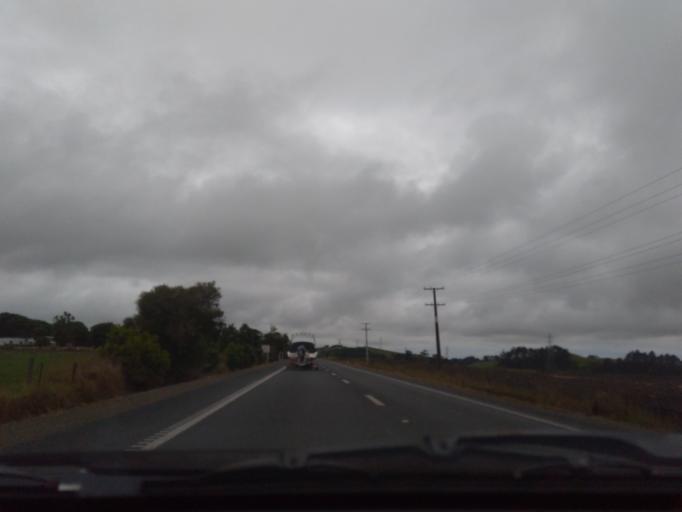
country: NZ
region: Northland
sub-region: Whangarei
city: Ruakaka
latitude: -36.0233
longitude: 174.4178
